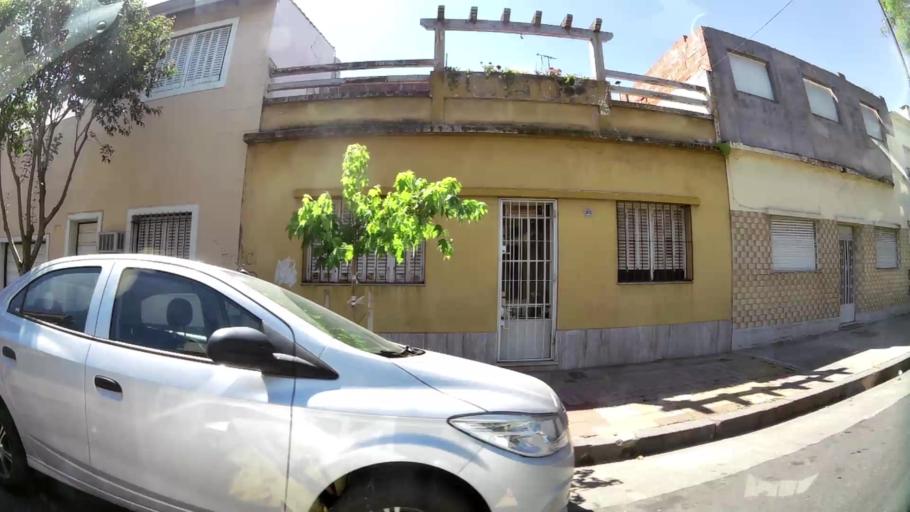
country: AR
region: Buenos Aires F.D.
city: Villa Santa Rita
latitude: -34.6352
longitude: -58.4515
